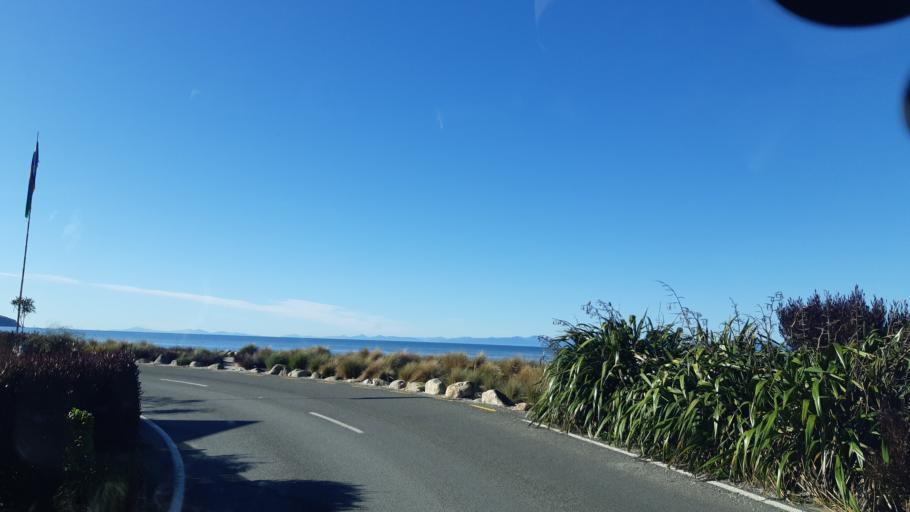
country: NZ
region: Tasman
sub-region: Tasman District
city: Motueka
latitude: -41.0090
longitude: 173.0080
